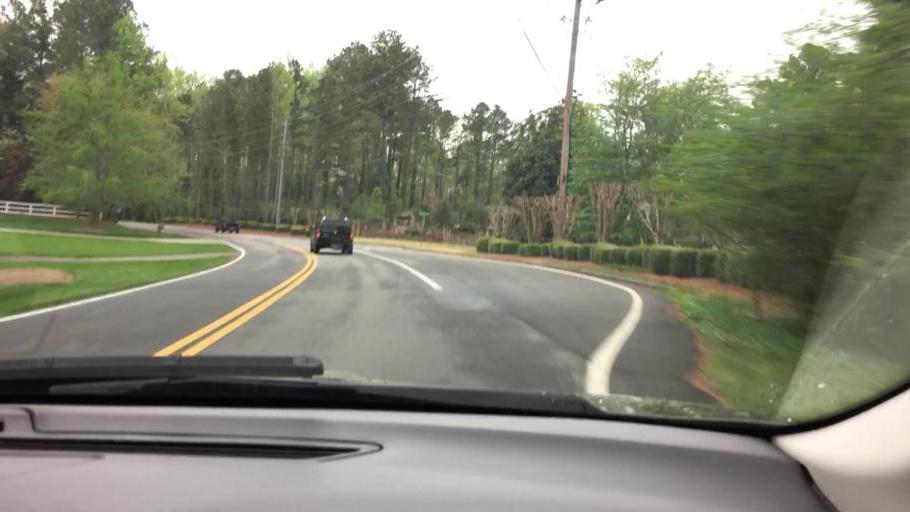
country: US
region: Georgia
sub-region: Fulton County
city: Milton
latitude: 34.1486
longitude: -84.2646
